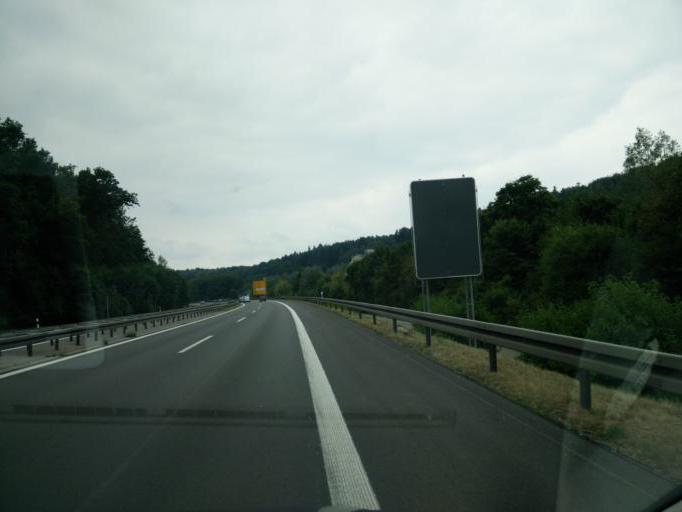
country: DE
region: Baden-Wuerttemberg
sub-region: Tuebingen Region
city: Dusslingen
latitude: 48.4828
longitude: 9.0666
